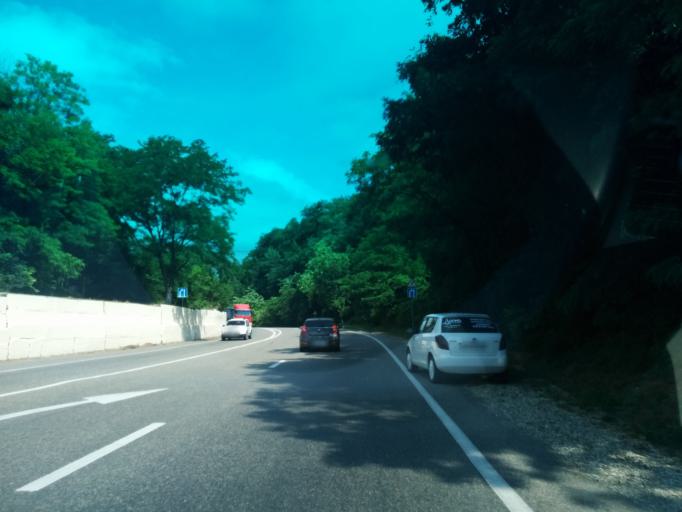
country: RU
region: Krasnodarskiy
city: Nebug
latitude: 44.1656
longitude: 38.9923
